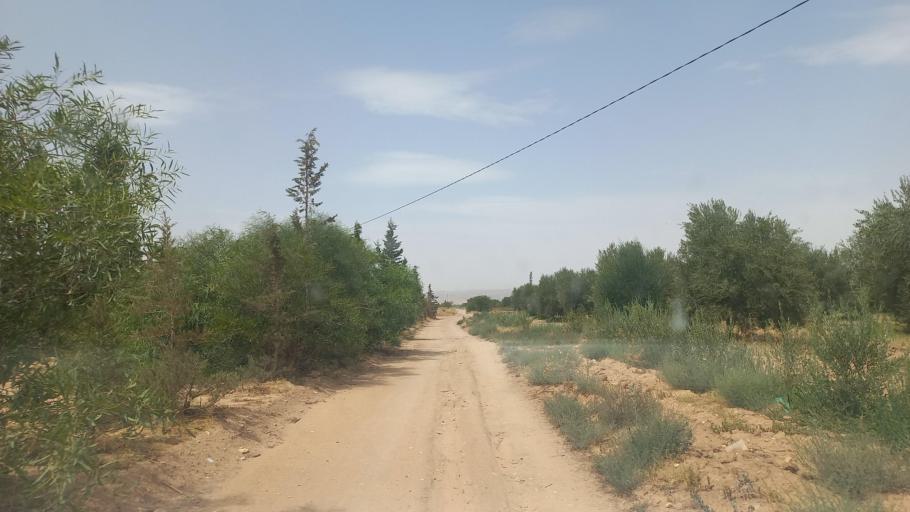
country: TN
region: Al Qasrayn
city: Kasserine
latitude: 35.2579
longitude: 9.0005
